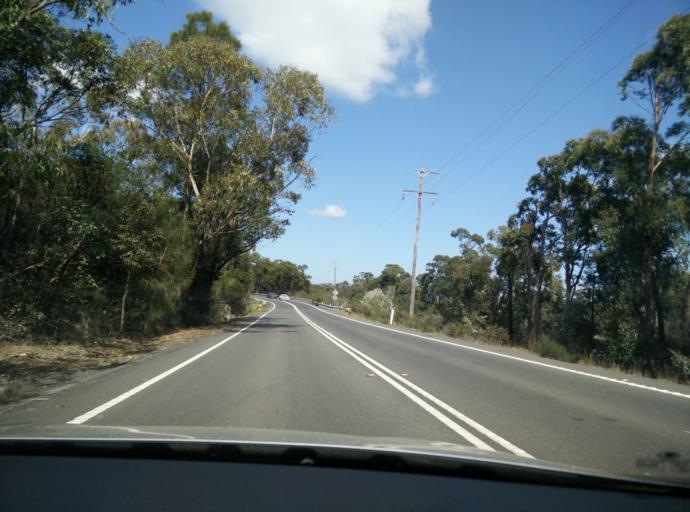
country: AU
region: New South Wales
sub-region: Gosford Shire
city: Point Clare
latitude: -33.4601
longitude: 151.2821
